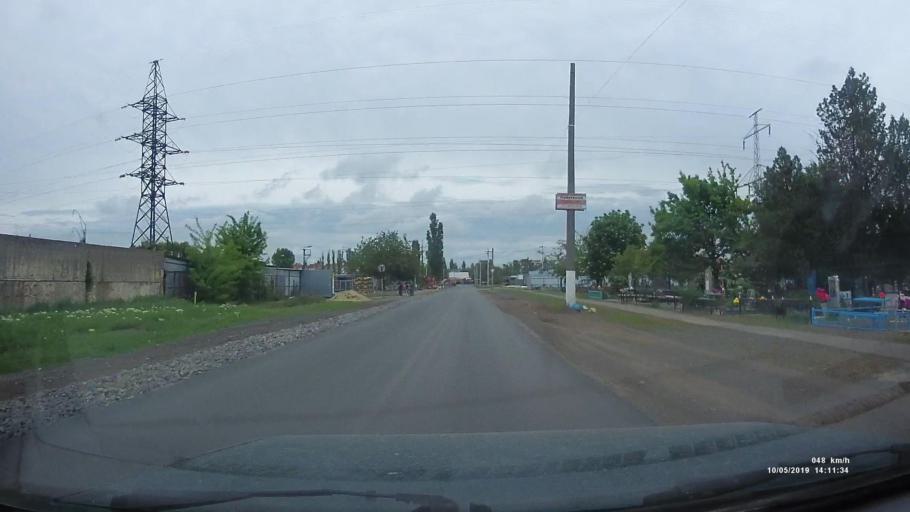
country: RU
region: Rostov
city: Azov
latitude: 47.0944
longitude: 39.4181
